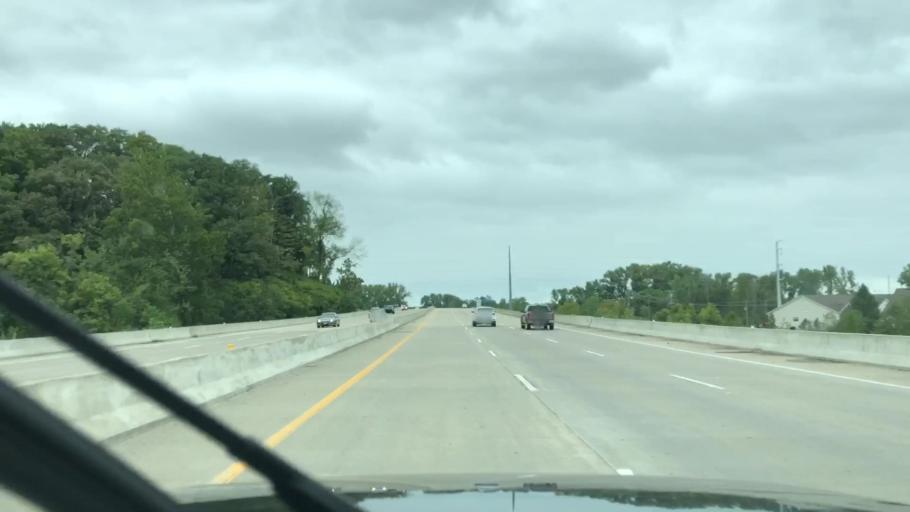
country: US
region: Missouri
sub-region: Saint Louis County
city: Maryland Heights
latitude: 38.6905
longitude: -90.4973
